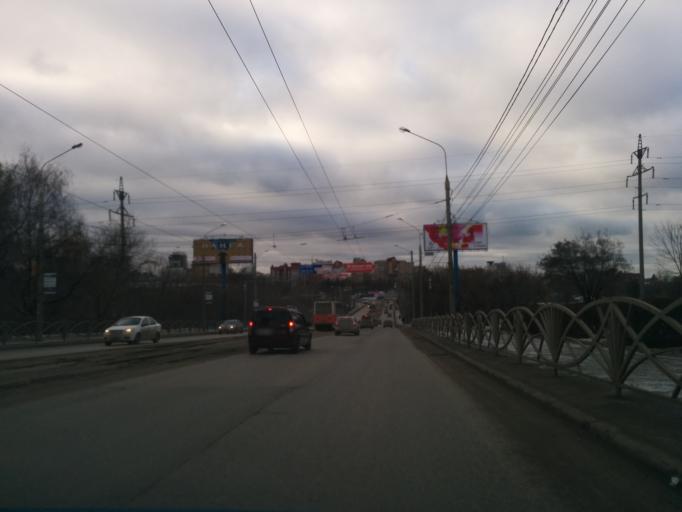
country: RU
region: Perm
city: Perm
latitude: 58.0184
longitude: 56.2714
